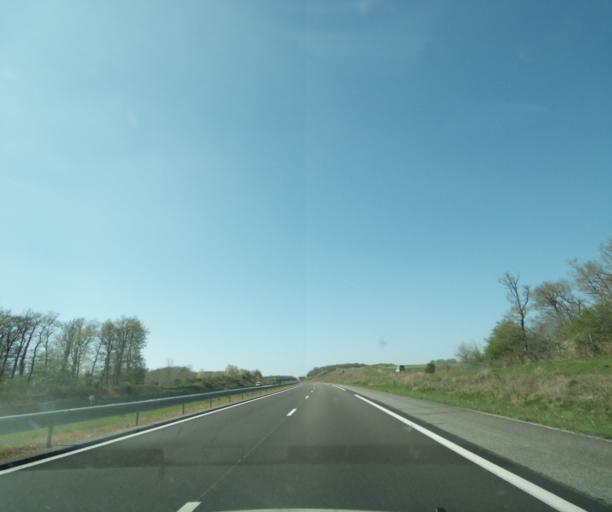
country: FR
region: Centre
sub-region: Departement du Loiret
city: Bonny-sur-Loire
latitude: 47.6082
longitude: 2.8288
